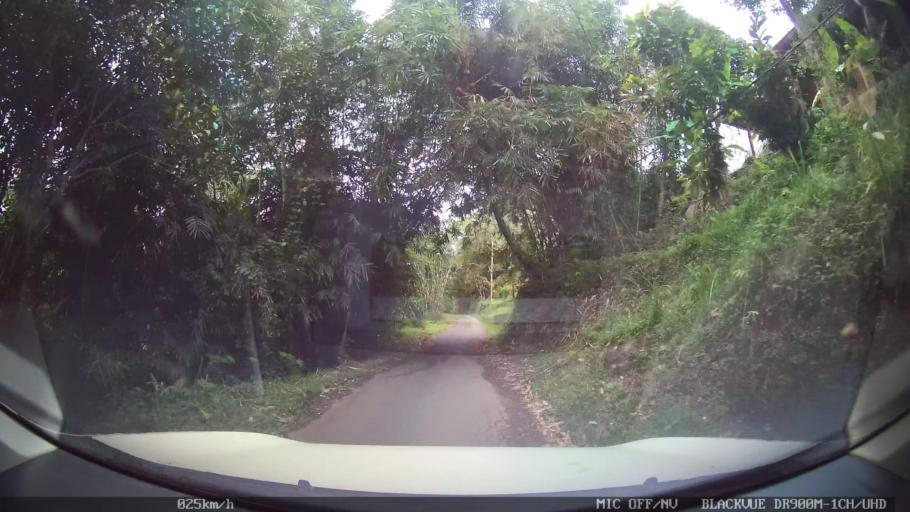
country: ID
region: Bali
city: Banjar Wangsian
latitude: -8.4596
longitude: 115.4163
